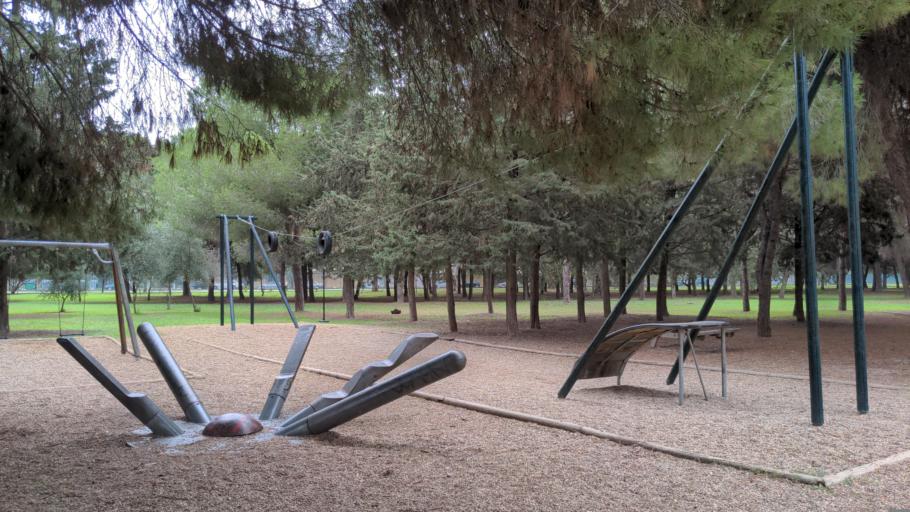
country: ES
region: Andalusia
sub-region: Provincia de Sevilla
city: Sevilla
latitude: 37.3928
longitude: -5.9284
